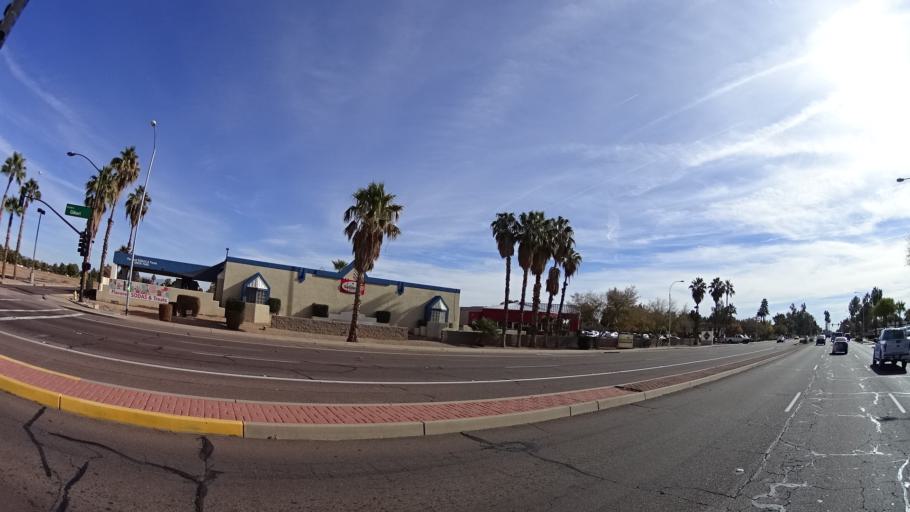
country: US
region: Arizona
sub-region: Maricopa County
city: Gilbert
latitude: 33.3736
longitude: -111.7902
